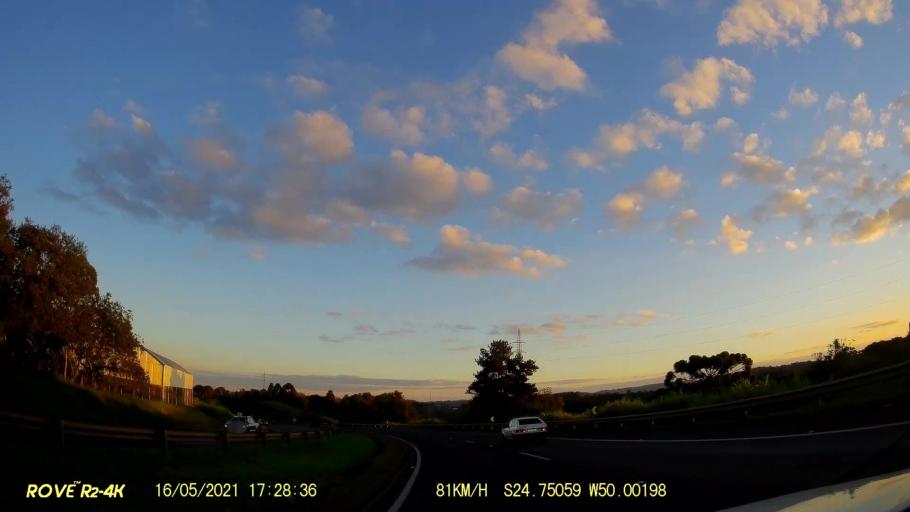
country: BR
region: Parana
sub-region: Castro
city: Castro
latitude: -24.7506
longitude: -50.0021
